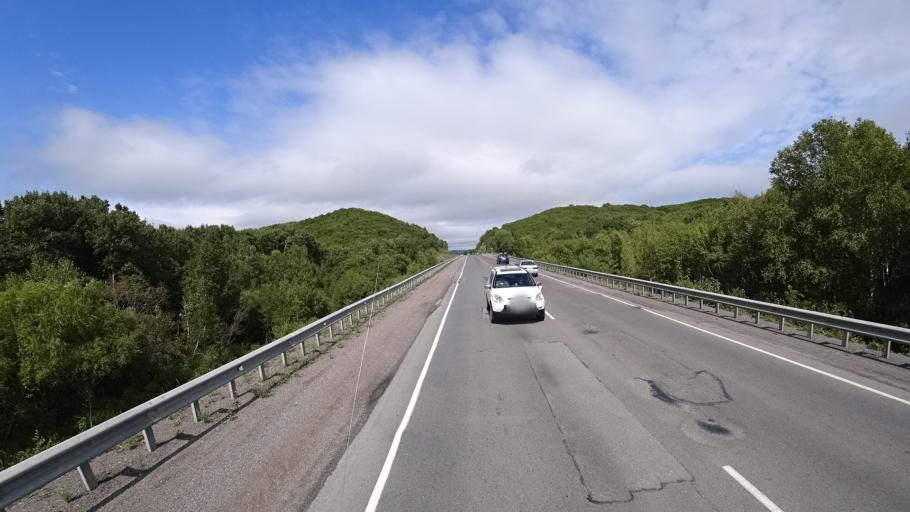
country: RU
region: Primorskiy
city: Lyalichi
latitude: 44.1249
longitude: 132.4233
